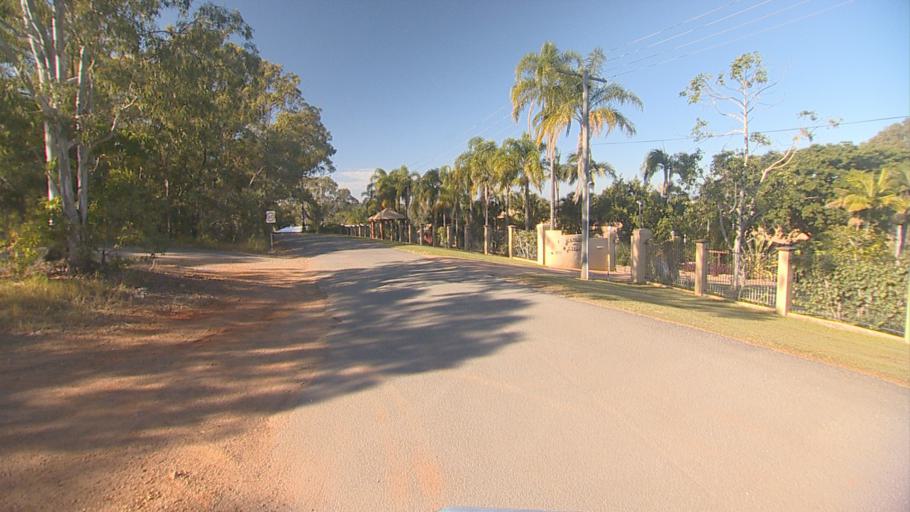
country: AU
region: Queensland
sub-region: Gold Coast
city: Yatala
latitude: -27.6877
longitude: 153.2667
